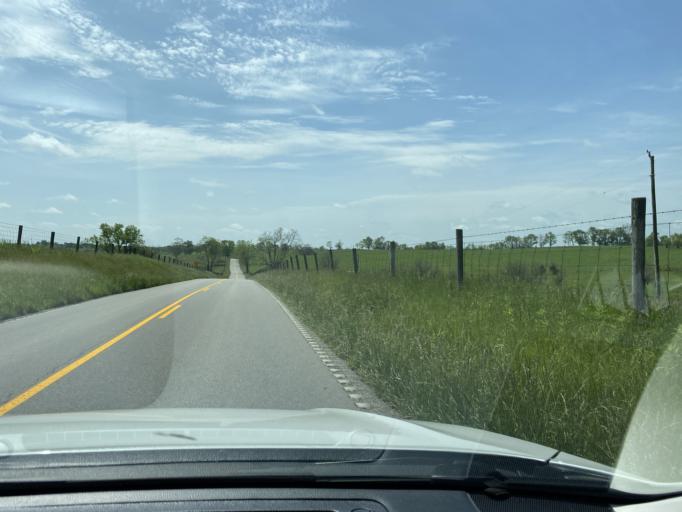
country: US
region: Kentucky
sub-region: Scott County
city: Georgetown
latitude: 38.2502
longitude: -84.5889
